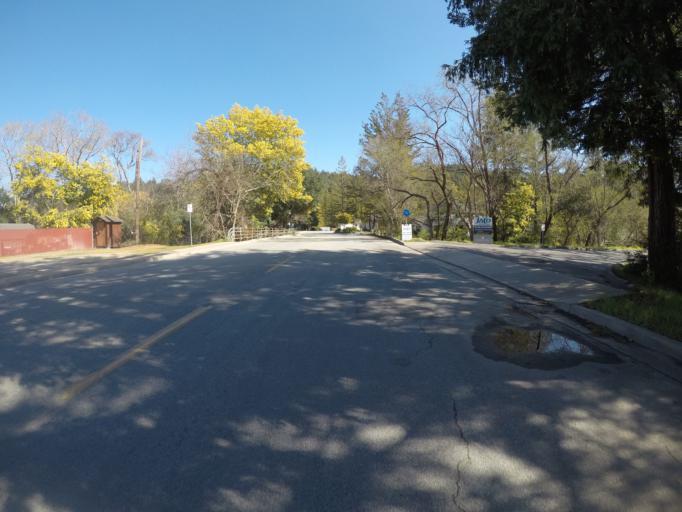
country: US
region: California
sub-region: Santa Cruz County
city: Scotts Valley
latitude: 37.0505
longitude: -122.0135
